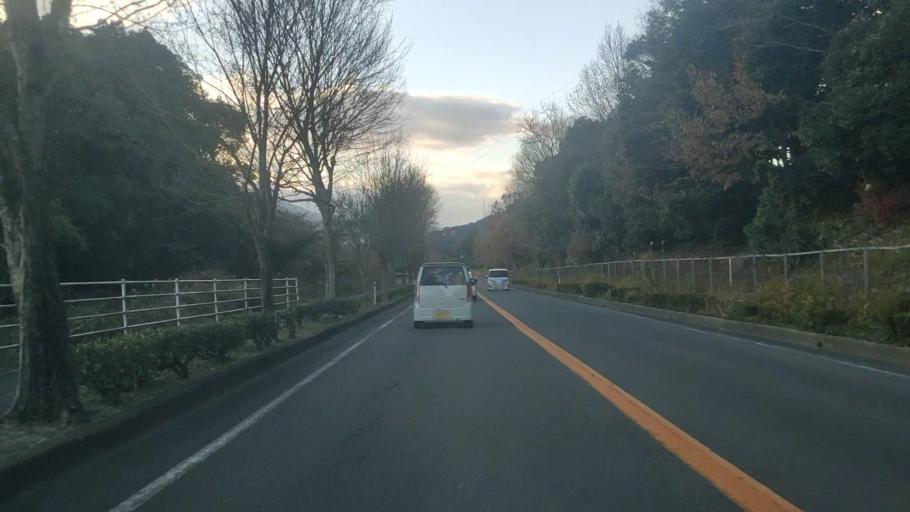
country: JP
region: Saga Prefecture
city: Saga-shi
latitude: 33.2873
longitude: 130.1461
